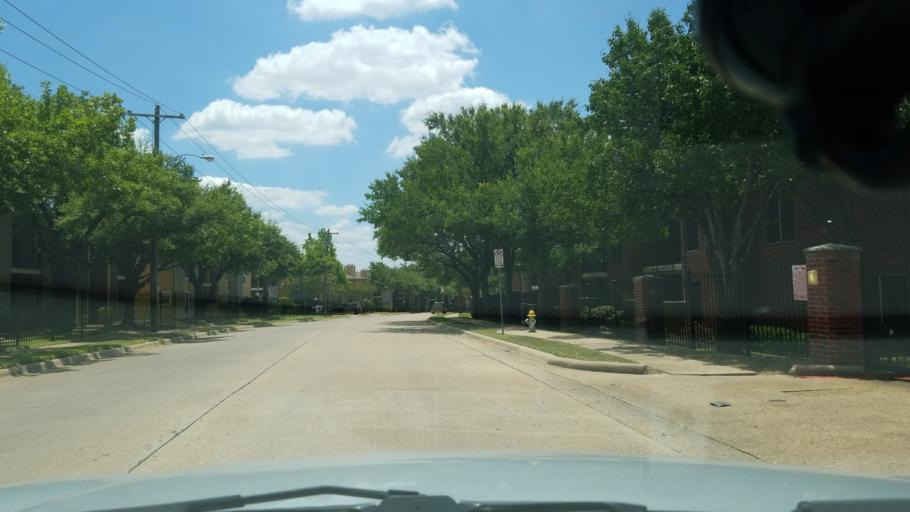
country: US
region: Texas
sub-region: Dallas County
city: Duncanville
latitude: 32.6761
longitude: -96.8795
